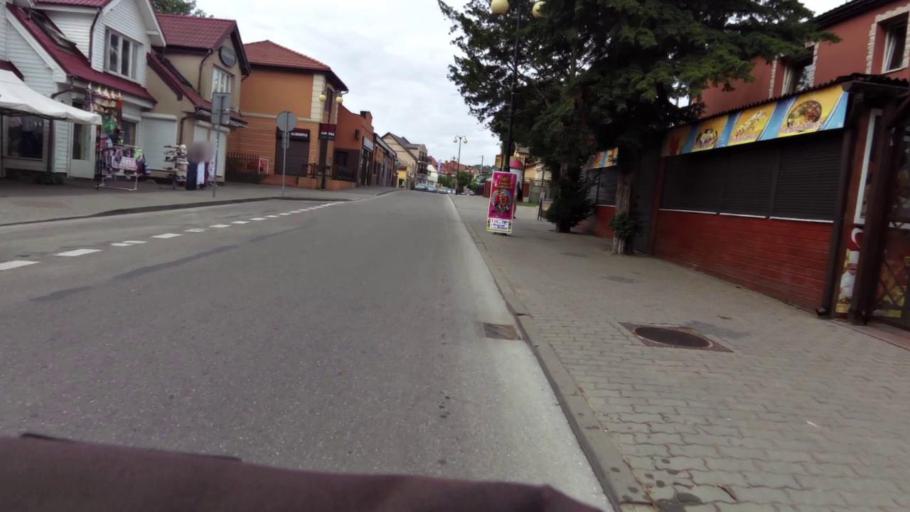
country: PL
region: West Pomeranian Voivodeship
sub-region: Powiat kamienski
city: Dziwnow
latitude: 54.0239
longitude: 14.7519
